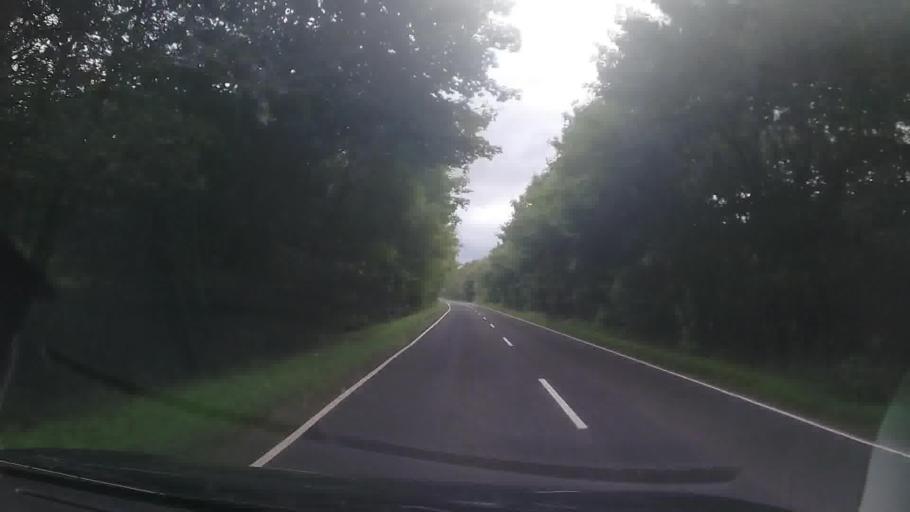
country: GB
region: Scotland
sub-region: Argyll and Bute
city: Garelochhead
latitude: 56.2425
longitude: -4.9514
